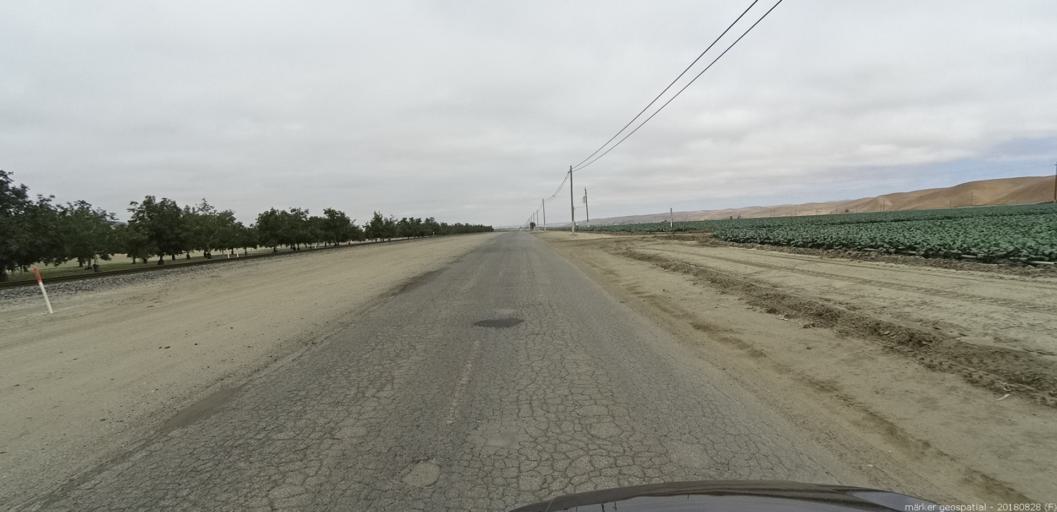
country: US
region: California
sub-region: San Luis Obispo County
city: Lake Nacimiento
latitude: 35.9731
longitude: -120.8750
